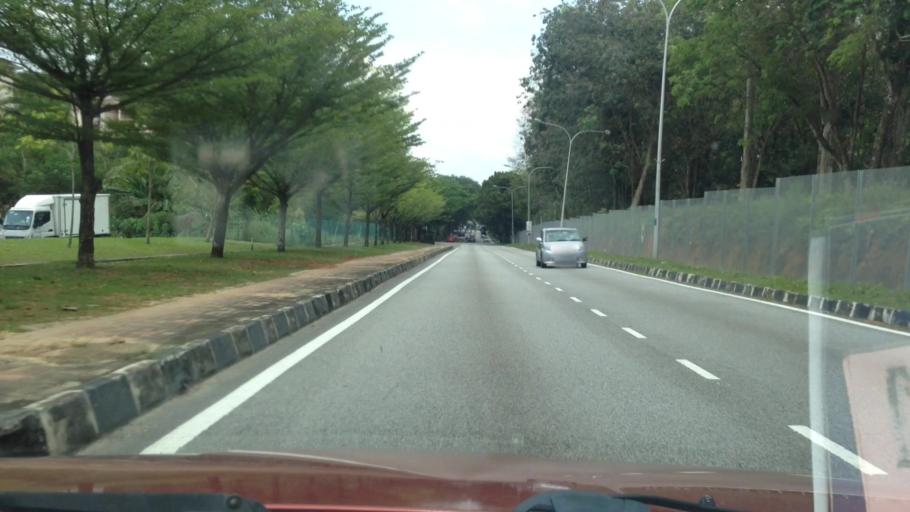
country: MY
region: Selangor
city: Kampung Baru Subang
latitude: 3.1679
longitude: 101.5513
